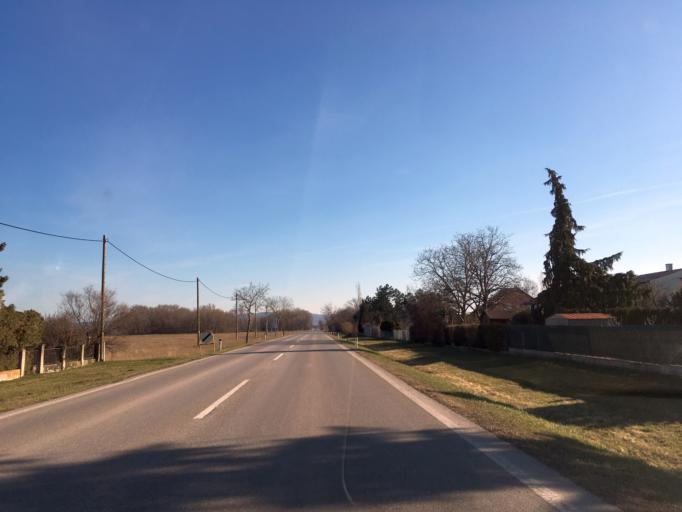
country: AT
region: Lower Austria
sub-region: Politischer Bezirk Baden
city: Ebreichsdorf
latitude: 47.9456
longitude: 16.4107
